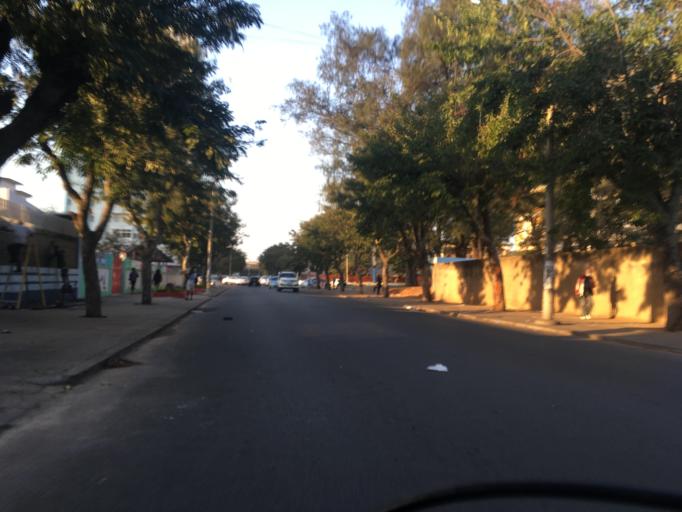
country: MZ
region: Maputo City
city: Maputo
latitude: -25.9671
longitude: 32.5940
